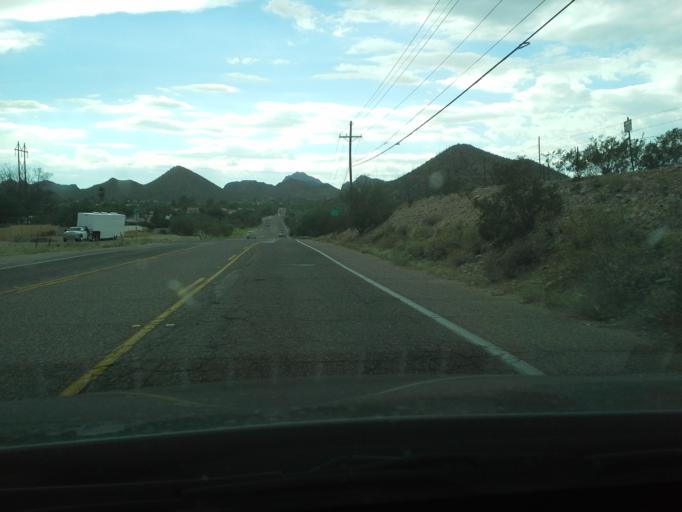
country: US
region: Arizona
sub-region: Pima County
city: South Tucson
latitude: 32.2069
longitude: -111.0139
